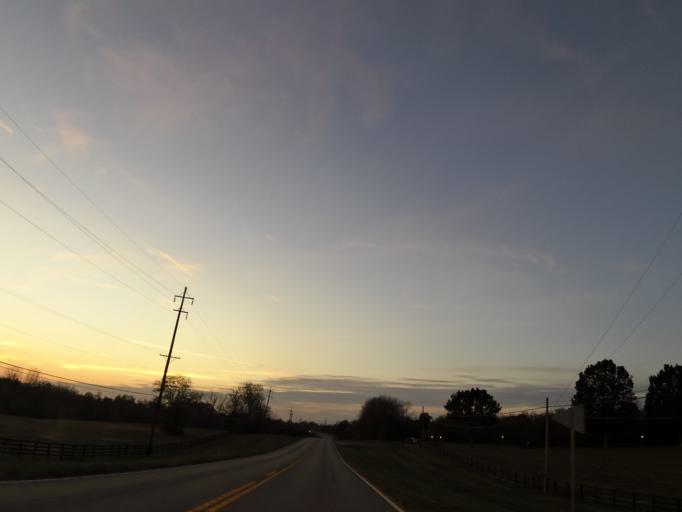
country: US
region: Kentucky
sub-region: Fayette County
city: Lexington-Fayette
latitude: 38.0378
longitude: -84.4034
